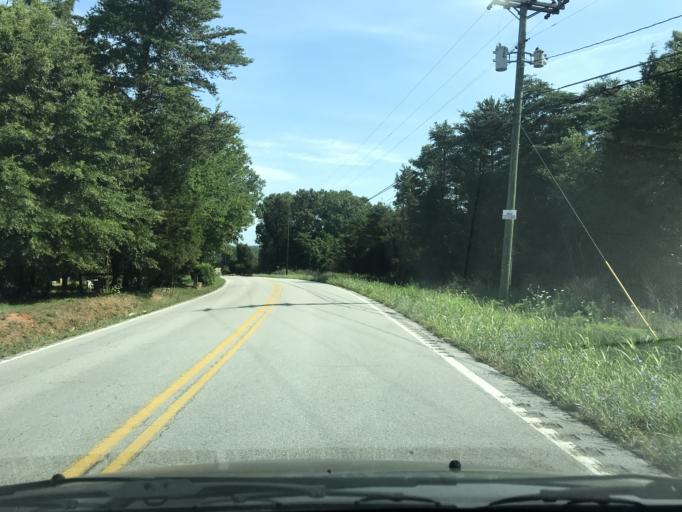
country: US
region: Tennessee
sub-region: Hamilton County
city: Lakesite
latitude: 35.2773
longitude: -85.0542
